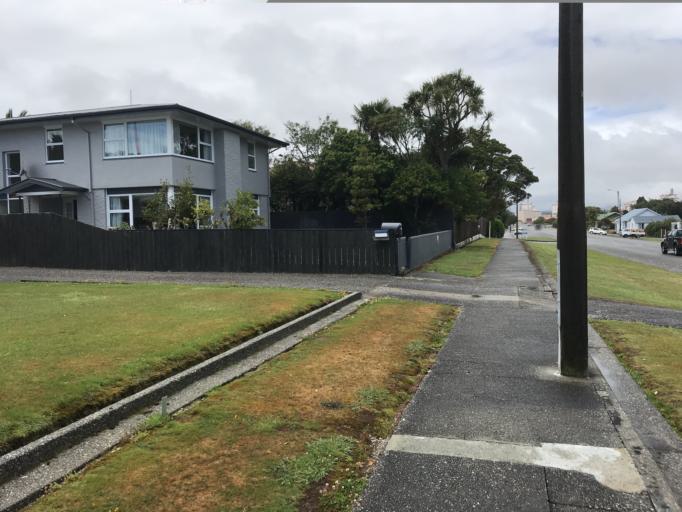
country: NZ
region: West Coast
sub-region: Westland District
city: Hokitika
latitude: -42.7187
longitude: 170.9695
